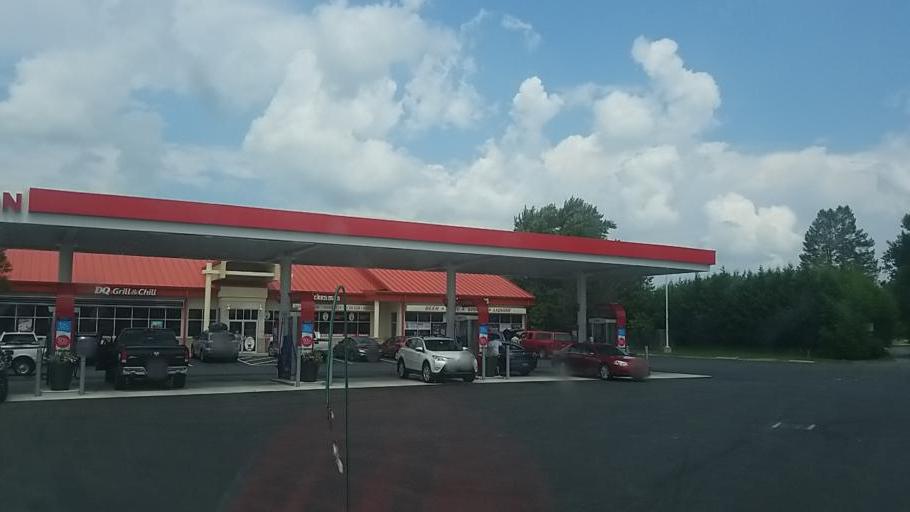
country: US
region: Delaware
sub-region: Sussex County
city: Milford
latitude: 38.9611
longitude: -75.4292
